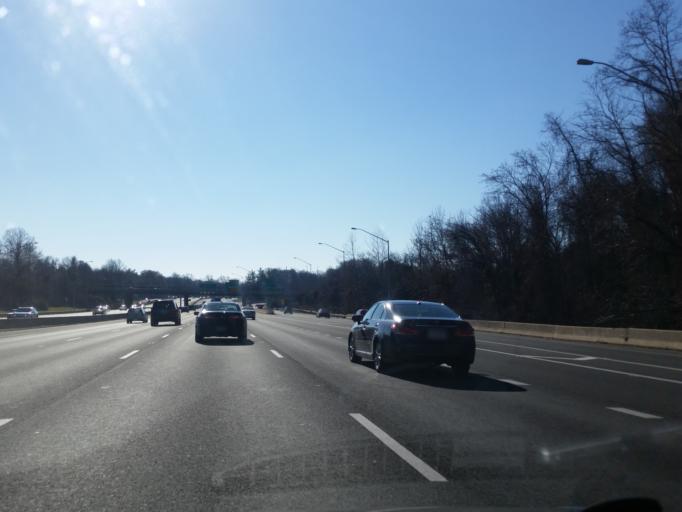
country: US
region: Maryland
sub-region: Montgomery County
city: Cabin John
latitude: 38.9940
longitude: -77.1580
